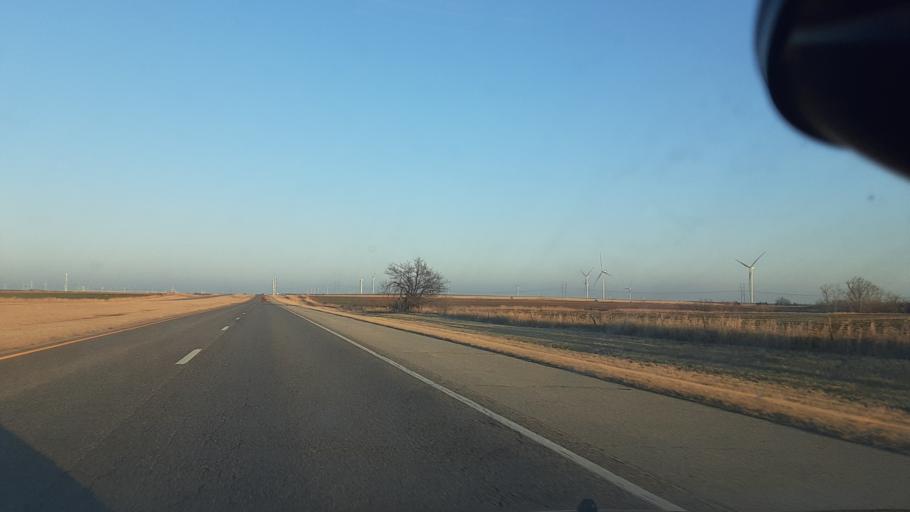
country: US
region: Oklahoma
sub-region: Noble County
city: Perry
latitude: 36.3975
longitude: -97.4934
